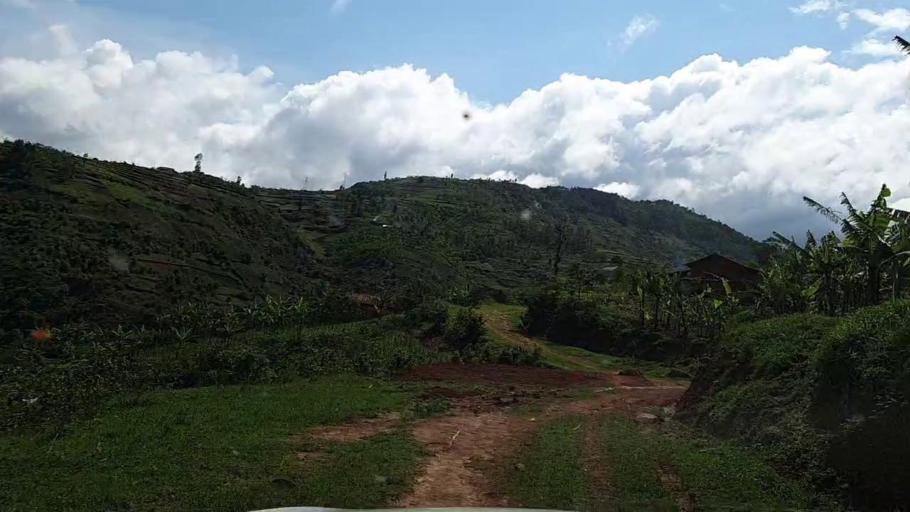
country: RW
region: Southern Province
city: Gikongoro
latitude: -2.3602
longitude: 29.5394
